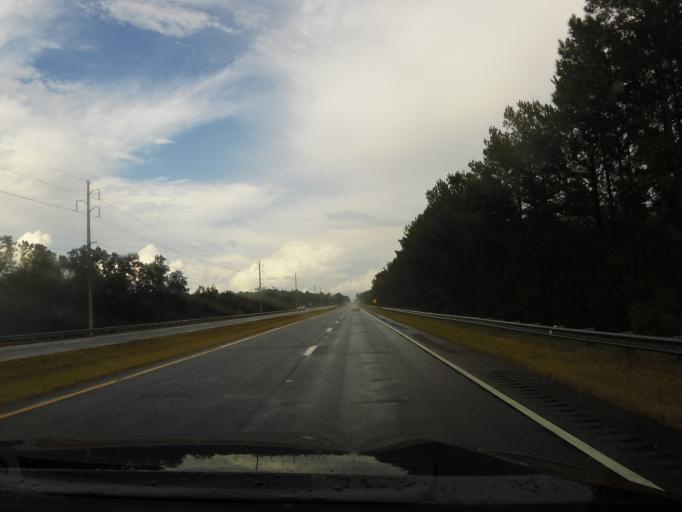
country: US
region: Georgia
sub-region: Long County
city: Ludowici
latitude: 31.7034
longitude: -81.7645
